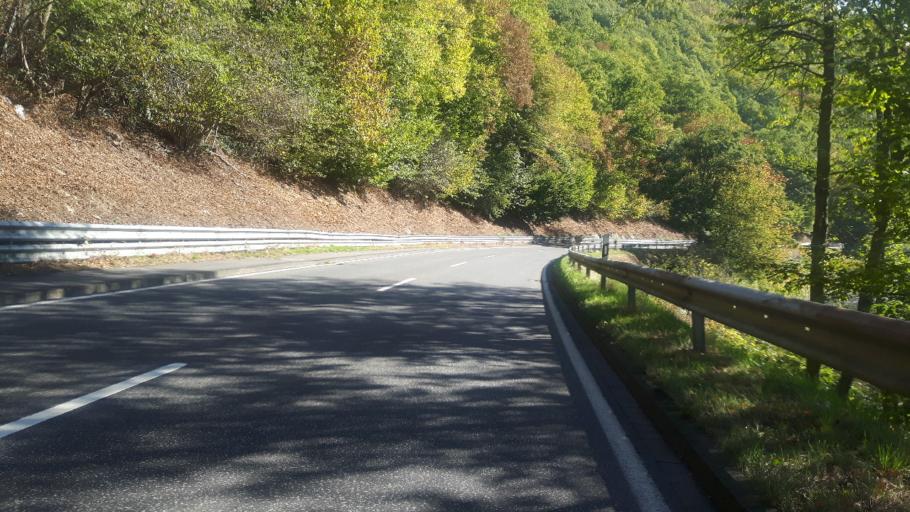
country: DE
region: Rheinland-Pfalz
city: Furthen
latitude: 50.7969
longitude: 7.6208
